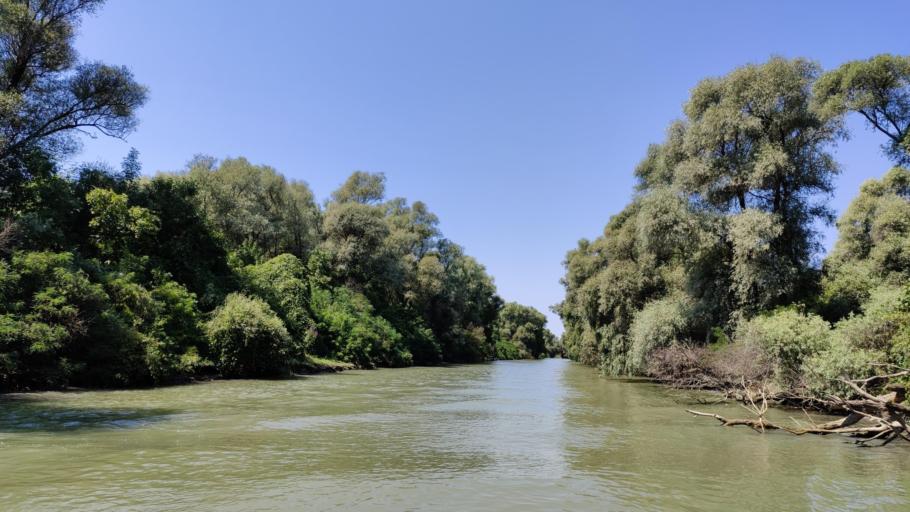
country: RO
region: Tulcea
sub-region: Comuna Pardina
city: Pardina
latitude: 45.2541
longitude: 28.9466
